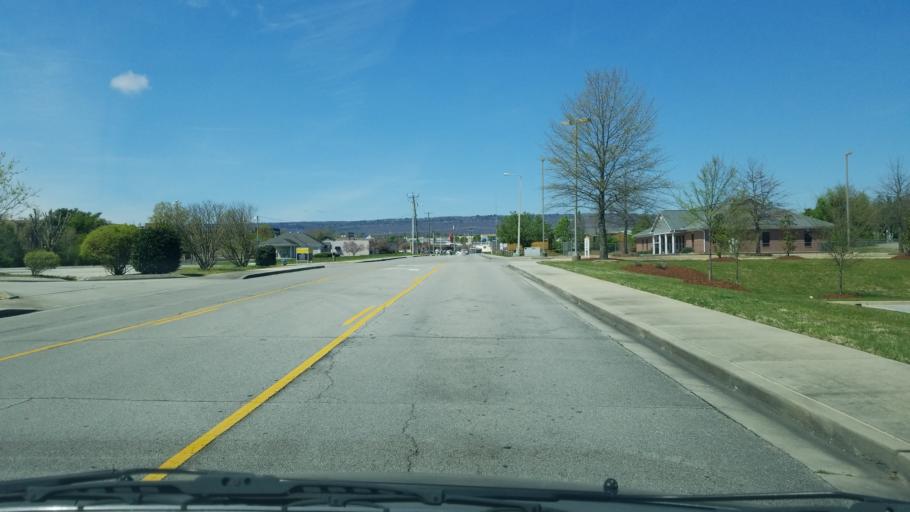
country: US
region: Tennessee
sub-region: Hamilton County
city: Red Bank
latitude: 35.1341
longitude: -85.2360
